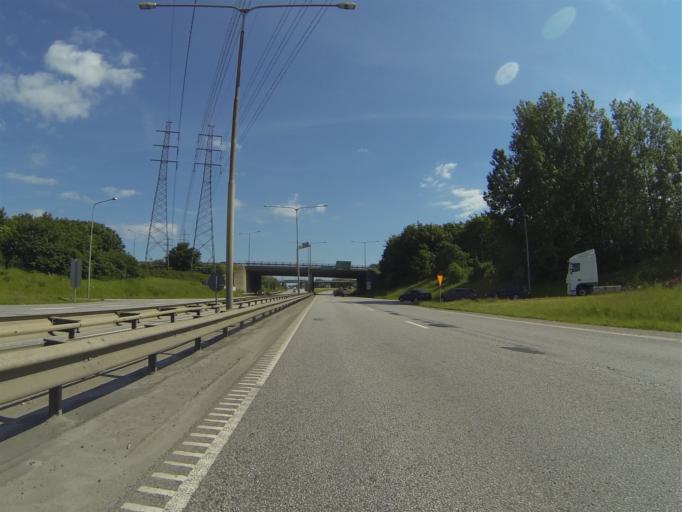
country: SE
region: Skane
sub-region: Burlovs Kommun
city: Arloev
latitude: 55.6235
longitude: 13.0571
